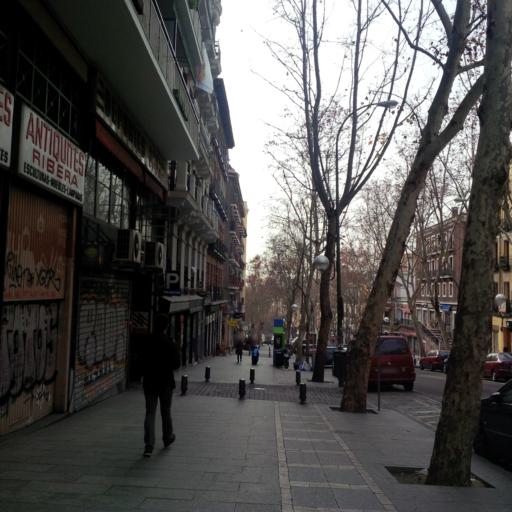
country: ES
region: Madrid
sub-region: Provincia de Madrid
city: Madrid
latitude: 40.4091
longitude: -3.7071
